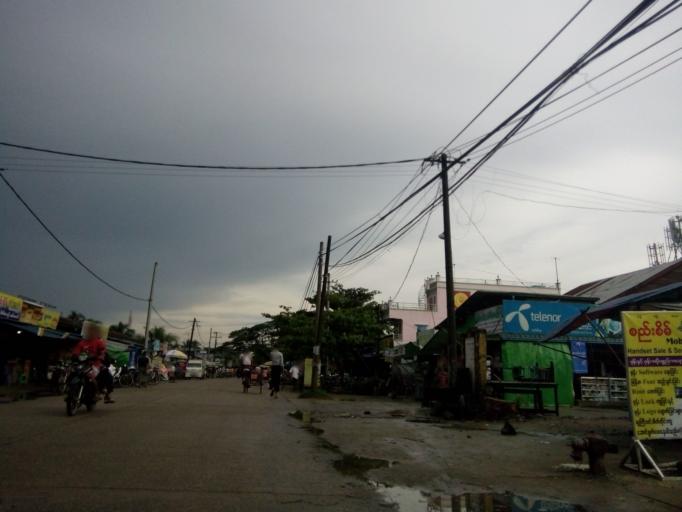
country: MM
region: Yangon
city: Yangon
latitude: 16.9237
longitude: 96.1591
